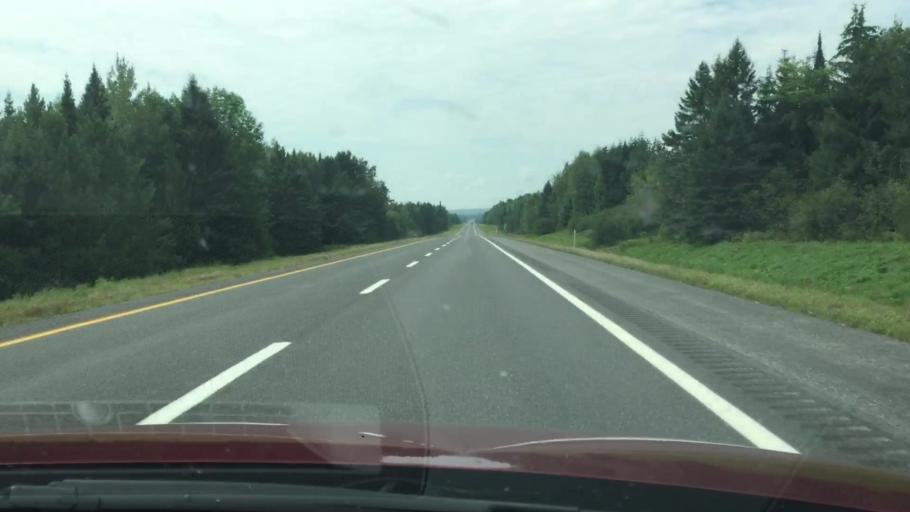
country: US
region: Maine
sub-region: Aroostook County
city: Houlton
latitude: 46.1415
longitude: -67.9580
